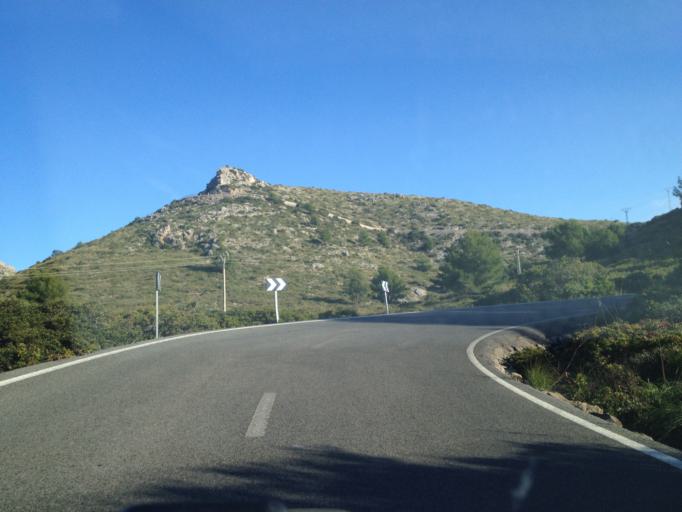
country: ES
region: Balearic Islands
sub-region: Illes Balears
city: Alcudia
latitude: 39.9148
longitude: 3.1041
